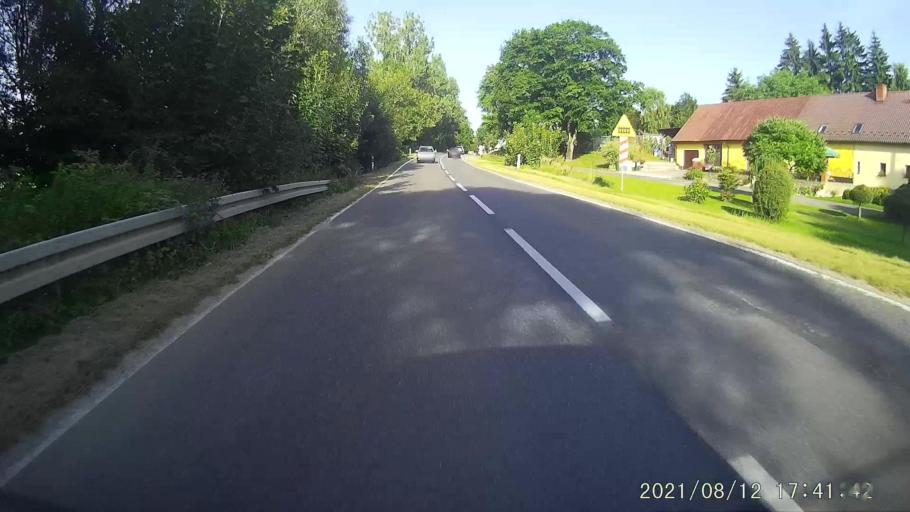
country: PL
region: Lower Silesian Voivodeship
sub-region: Powiat klodzki
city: Ladek-Zdroj
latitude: 50.3395
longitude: 16.8229
